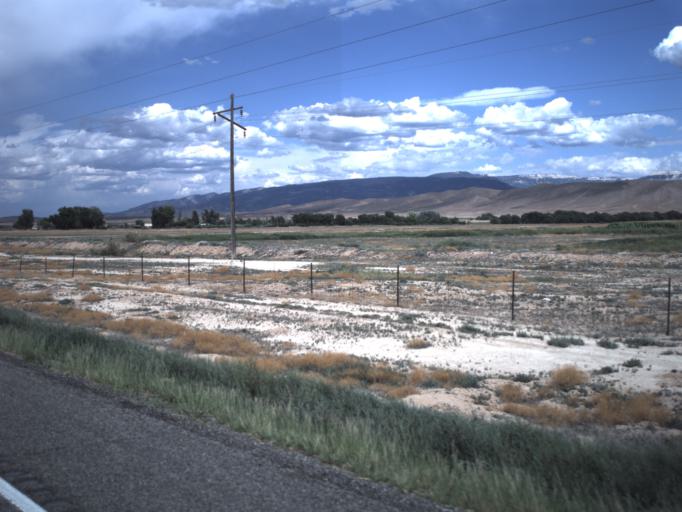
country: US
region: Utah
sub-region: Sevier County
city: Salina
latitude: 39.0382
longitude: -111.8274
